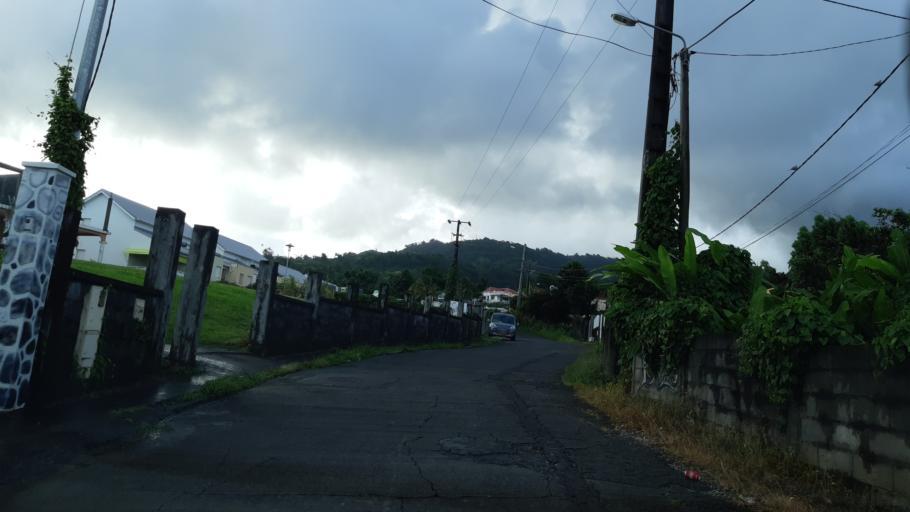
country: GP
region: Guadeloupe
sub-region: Guadeloupe
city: Trois-Rivieres
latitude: 15.9791
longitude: -61.6429
